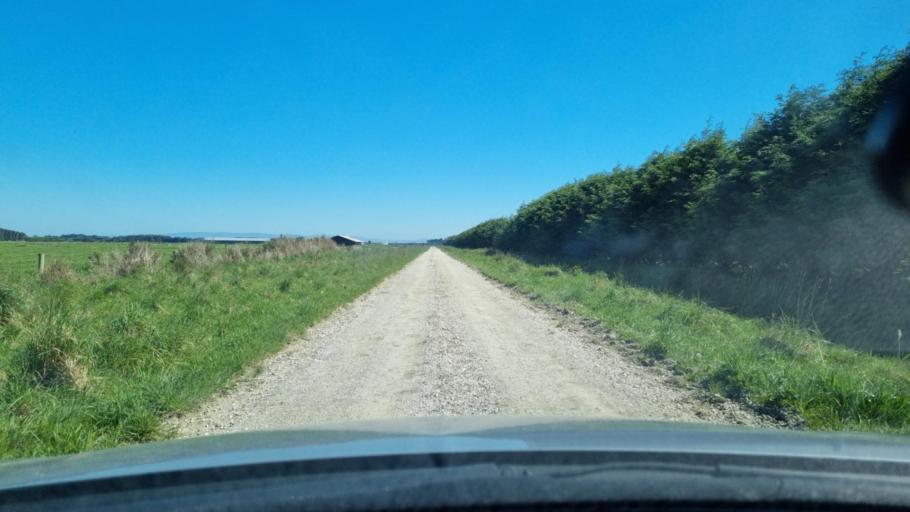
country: NZ
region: Southland
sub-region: Invercargill City
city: Invercargill
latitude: -46.4257
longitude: 168.3175
